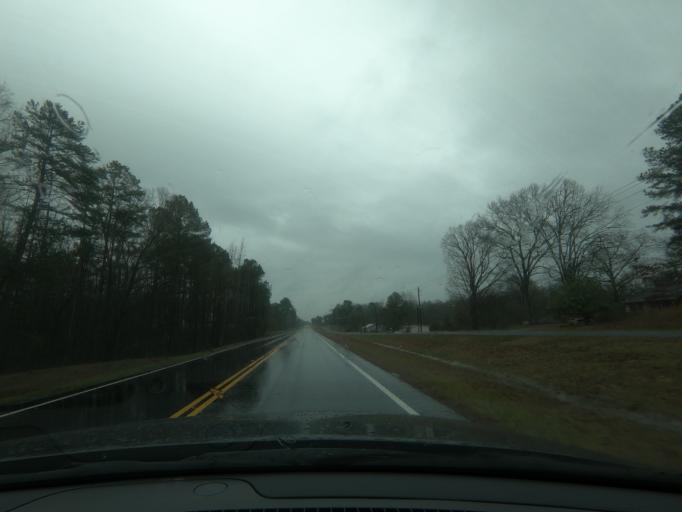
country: US
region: Georgia
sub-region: Bartow County
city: Adairsville
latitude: 34.3070
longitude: -84.8866
